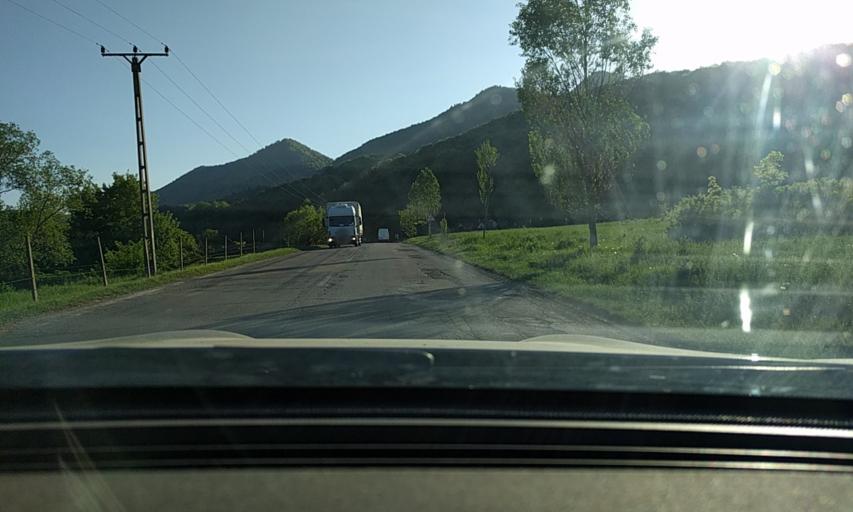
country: RO
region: Bacau
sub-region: Oras Slanic-Moldova
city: Slanic-Moldova
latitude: 46.1805
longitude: 26.4859
